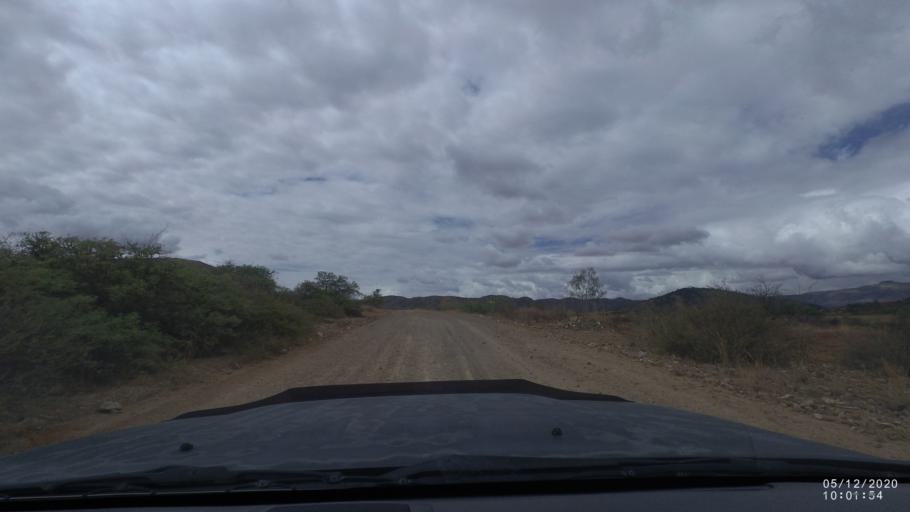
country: BO
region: Cochabamba
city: Sipe Sipe
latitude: -17.4455
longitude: -66.2872
